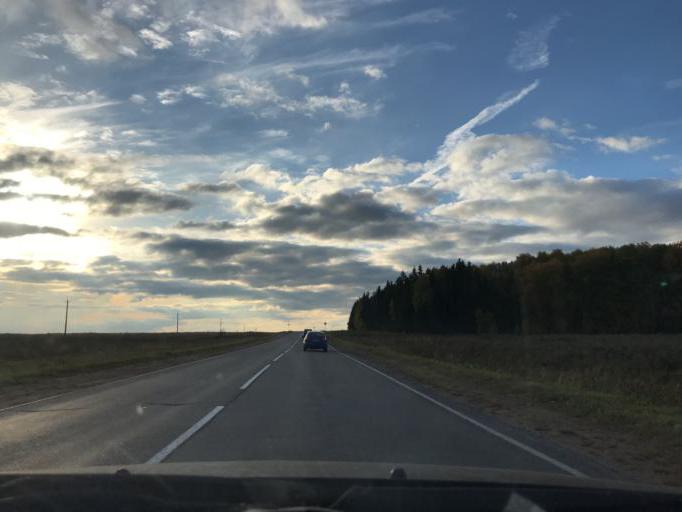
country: RU
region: Kaluga
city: Kurovskoye
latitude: 54.5289
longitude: 35.9395
